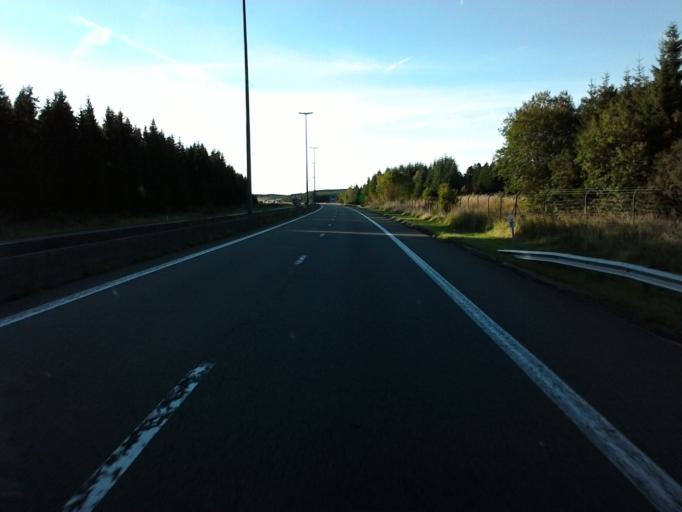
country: BE
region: Wallonia
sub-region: Province de Liege
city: Lierneux
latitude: 50.2399
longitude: 5.7529
